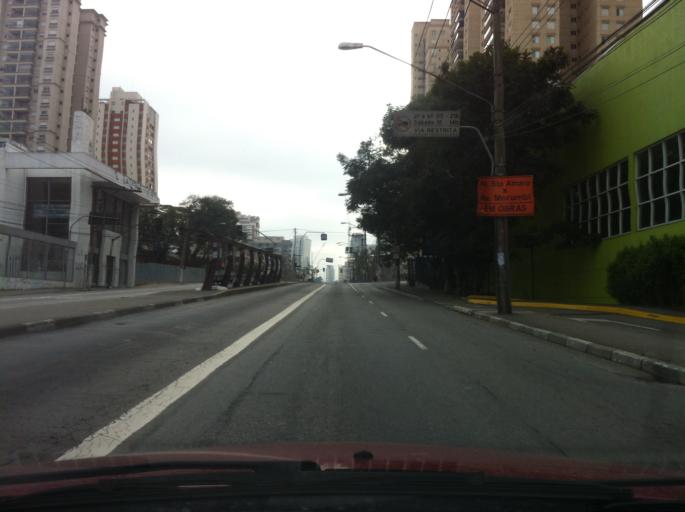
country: BR
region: Sao Paulo
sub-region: Diadema
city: Diadema
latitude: -23.6270
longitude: -46.6877
